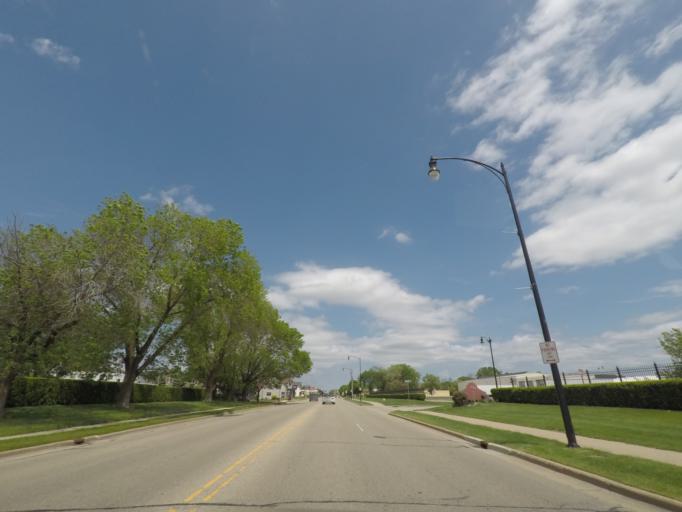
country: US
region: Wisconsin
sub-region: Rock County
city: Beloit
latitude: 42.5038
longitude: -89.0379
